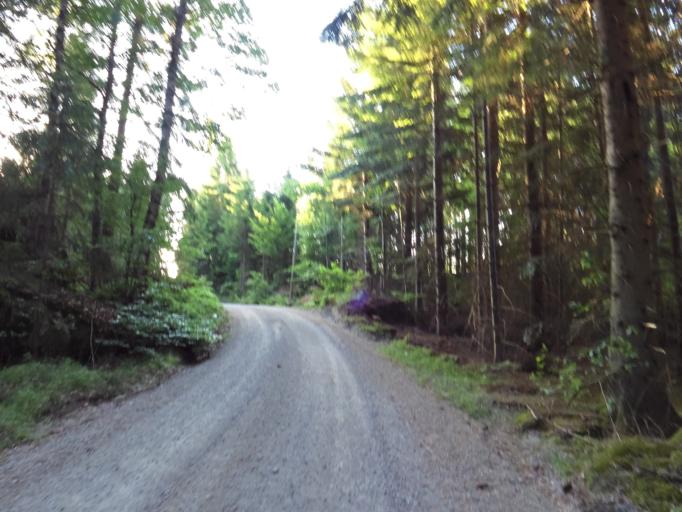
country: SE
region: Blekinge
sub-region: Olofstroms Kommun
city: Olofstroem
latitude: 56.4063
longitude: 14.5649
